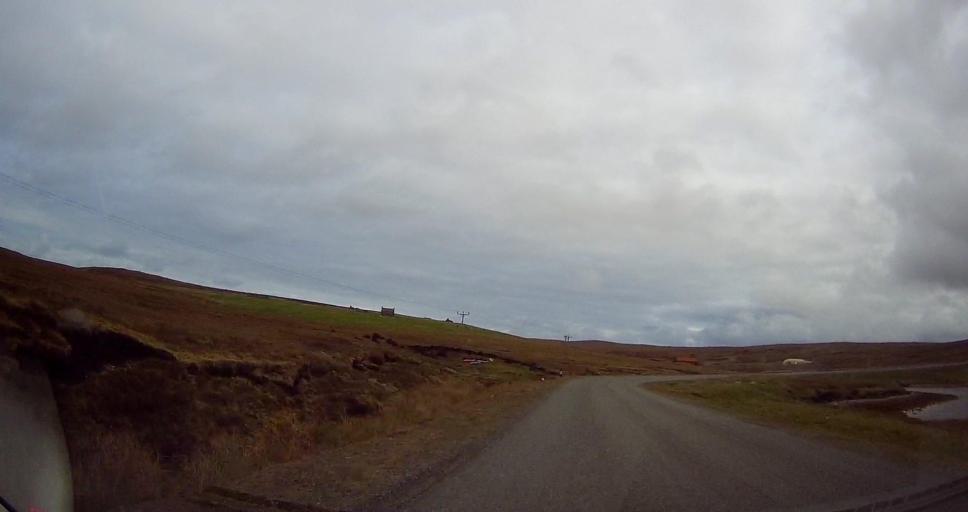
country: GB
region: Scotland
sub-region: Shetland Islands
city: Shetland
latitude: 60.6663
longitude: -1.0680
